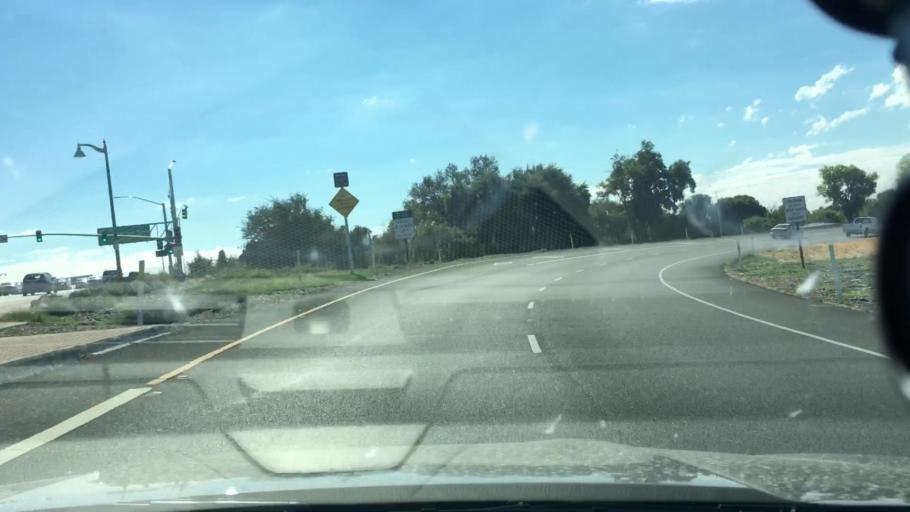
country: US
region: California
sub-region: Sacramento County
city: Rosemont
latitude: 38.5602
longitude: -121.3808
